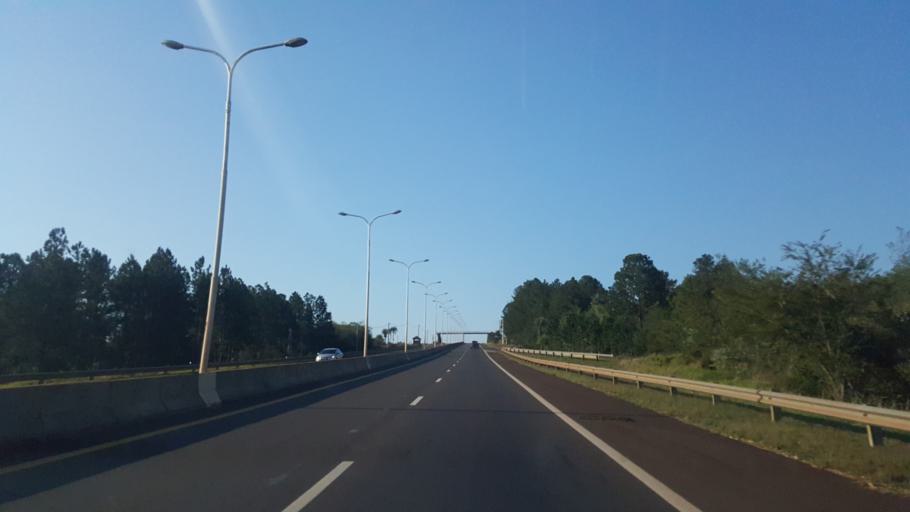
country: AR
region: Misiones
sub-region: Departamento de Candelaria
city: Loreto
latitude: -27.3042
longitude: -55.5391
